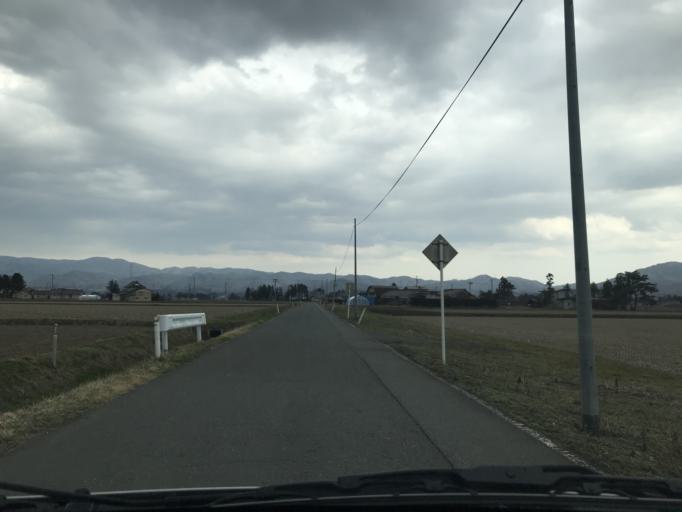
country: JP
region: Iwate
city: Mizusawa
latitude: 39.0767
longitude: 141.1442
